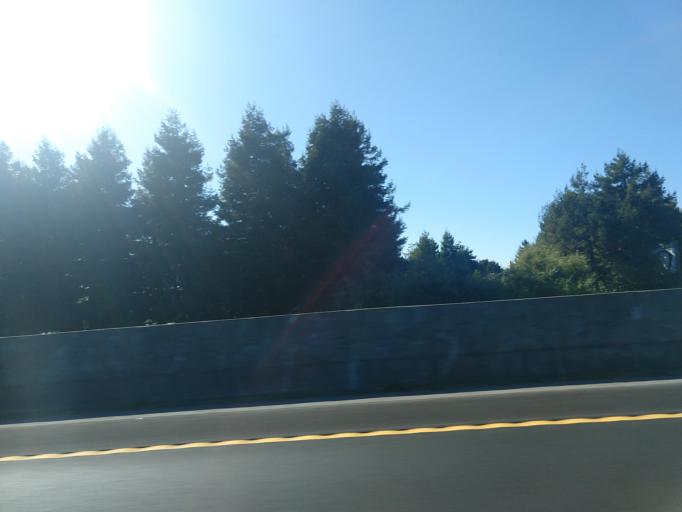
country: US
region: California
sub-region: Humboldt County
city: Fortuna
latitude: 40.5773
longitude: -124.1494
